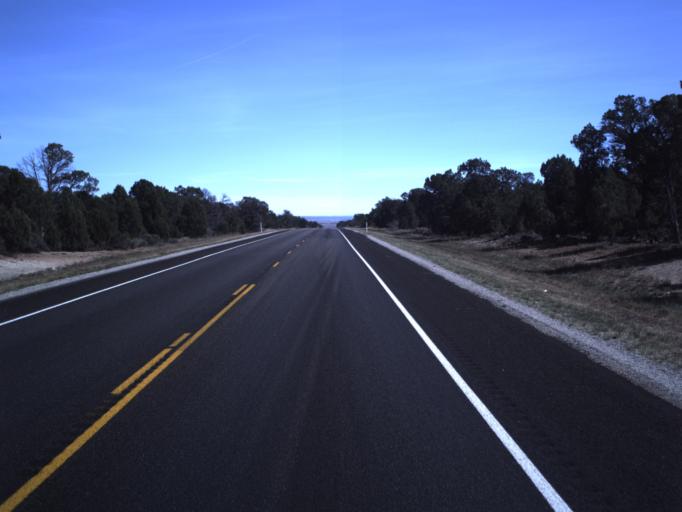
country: US
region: Colorado
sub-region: Dolores County
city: Dove Creek
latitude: 37.8311
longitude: -109.0930
